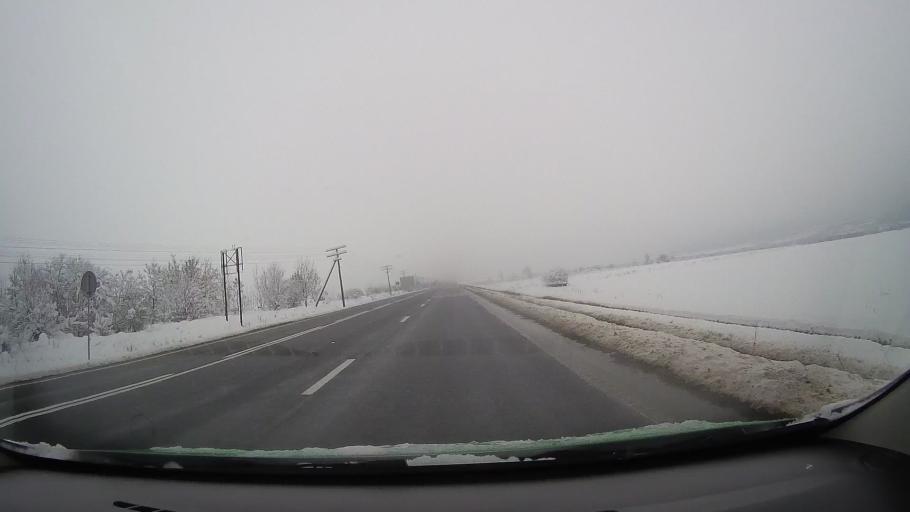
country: RO
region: Sibiu
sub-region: Oras Saliste
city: Saliste
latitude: 45.7989
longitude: 23.9035
